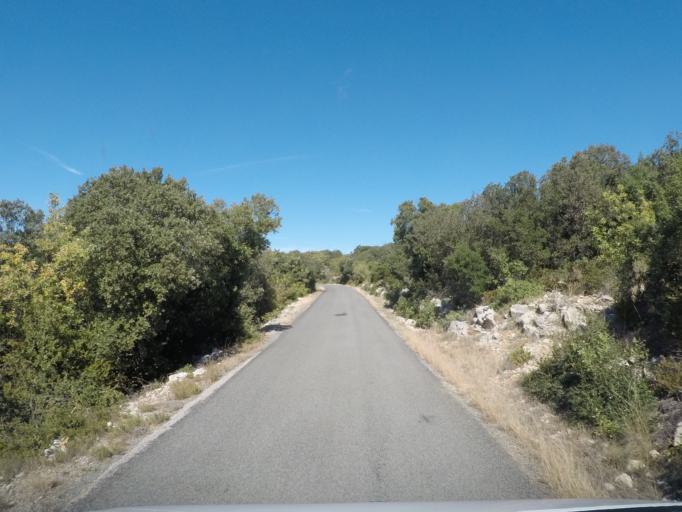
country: FR
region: Languedoc-Roussillon
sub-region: Departement de l'Herault
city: Vailhauques
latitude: 43.7233
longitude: 3.6764
